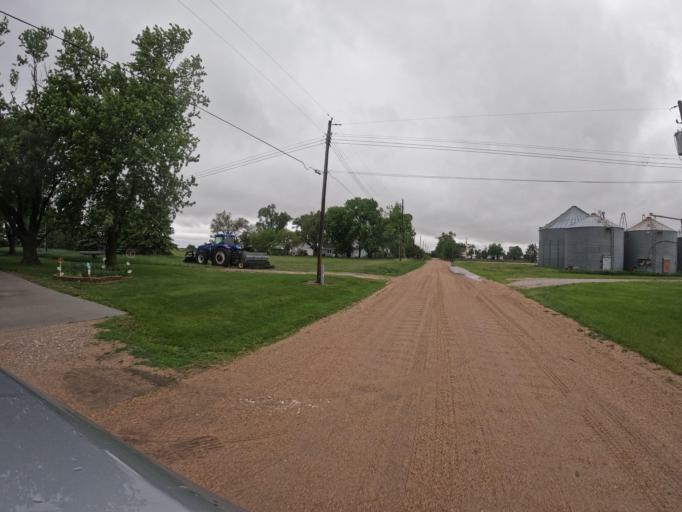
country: US
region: Nebraska
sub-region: Clay County
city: Harvard
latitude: 40.6280
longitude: -98.0968
